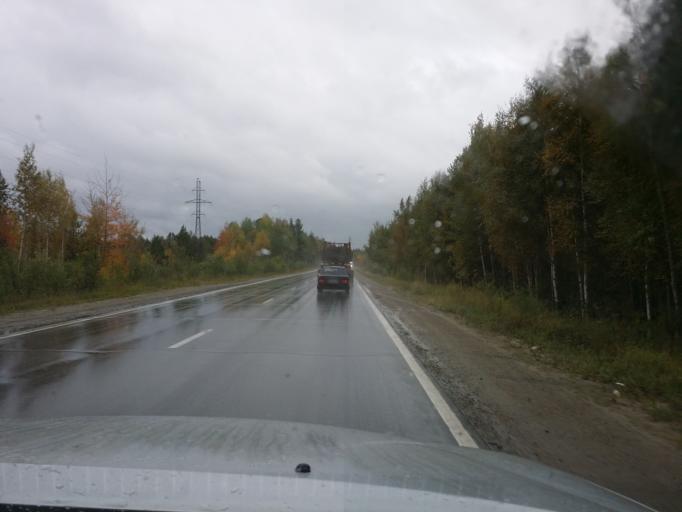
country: RU
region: Khanty-Mansiyskiy Avtonomnyy Okrug
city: Megion
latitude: 61.1456
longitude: 75.7539
